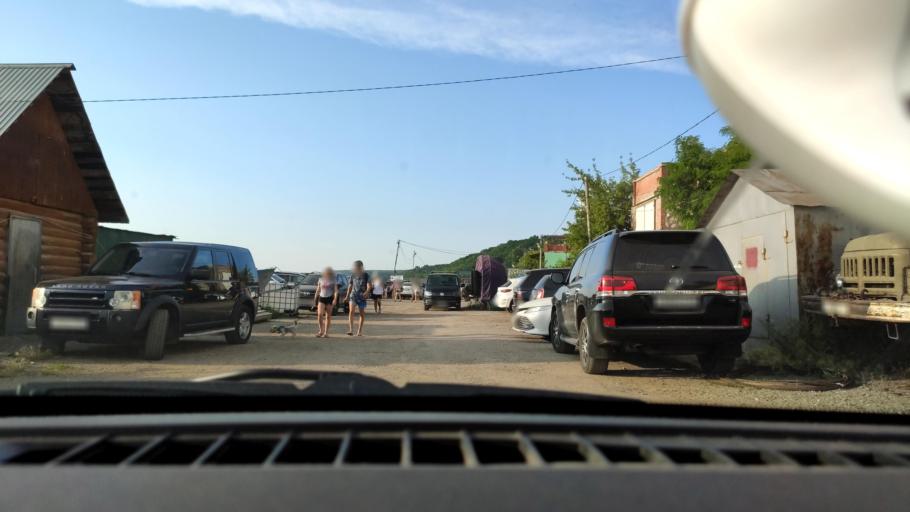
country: RU
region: Samara
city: Samara
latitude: 53.2790
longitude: 50.1872
